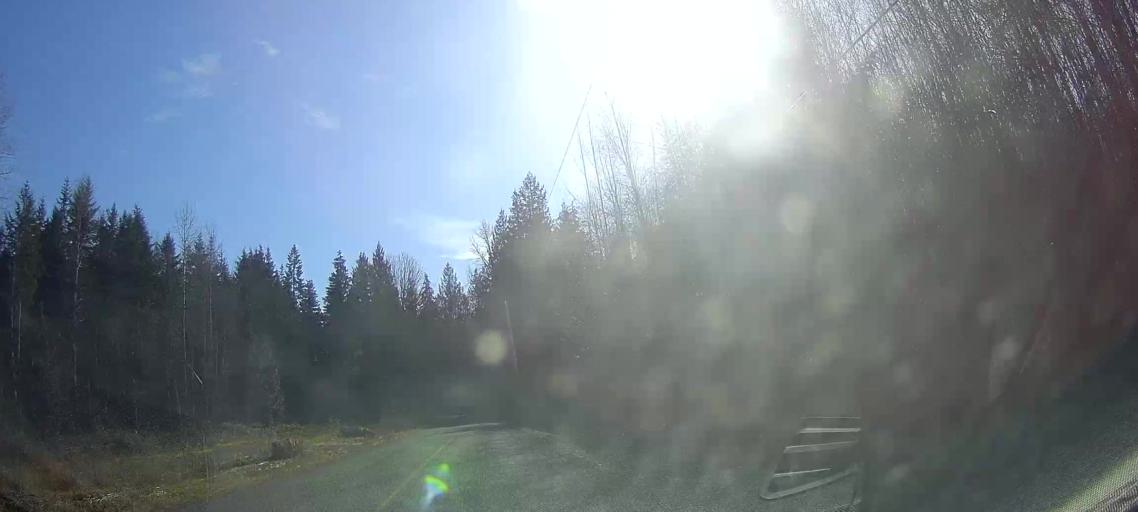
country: US
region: Washington
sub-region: Whatcom County
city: Sudden Valley
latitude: 48.6194
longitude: -122.3692
